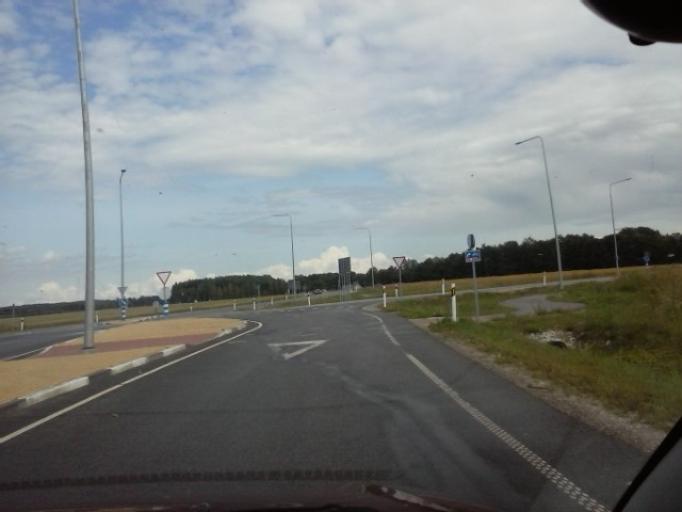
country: EE
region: Tartu
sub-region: Tartu linn
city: Tartu
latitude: 58.3605
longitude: 26.8921
